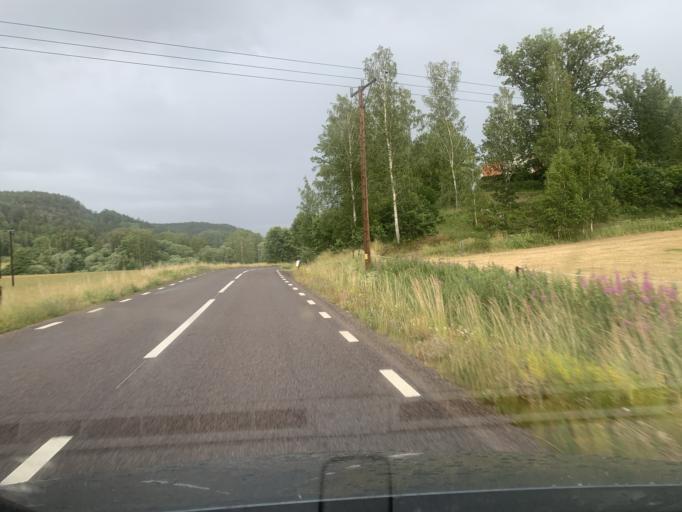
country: SE
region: Kalmar
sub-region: Vasterviks Kommun
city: Overum
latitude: 58.0168
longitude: 16.1622
